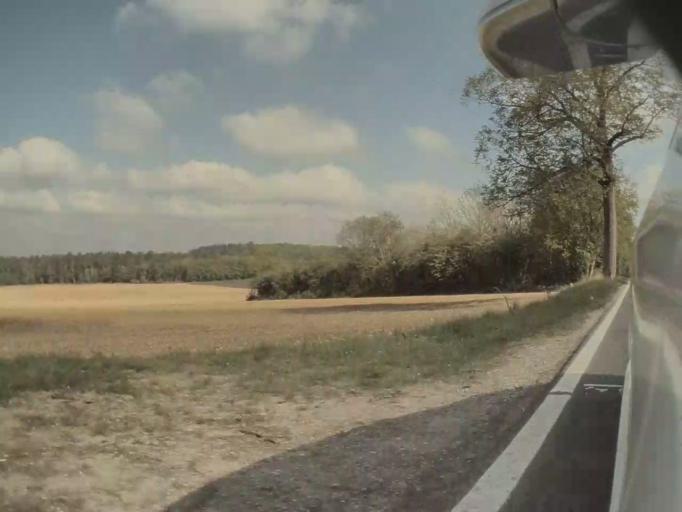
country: BE
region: Wallonia
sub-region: Province du Luxembourg
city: Tellin
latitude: 50.1005
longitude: 5.2311
